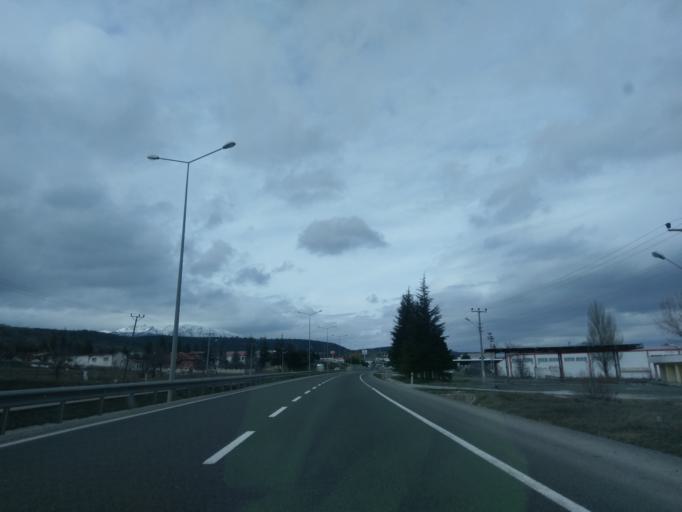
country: TR
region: Kuetahya
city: Kutahya
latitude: 39.3769
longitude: 30.0544
